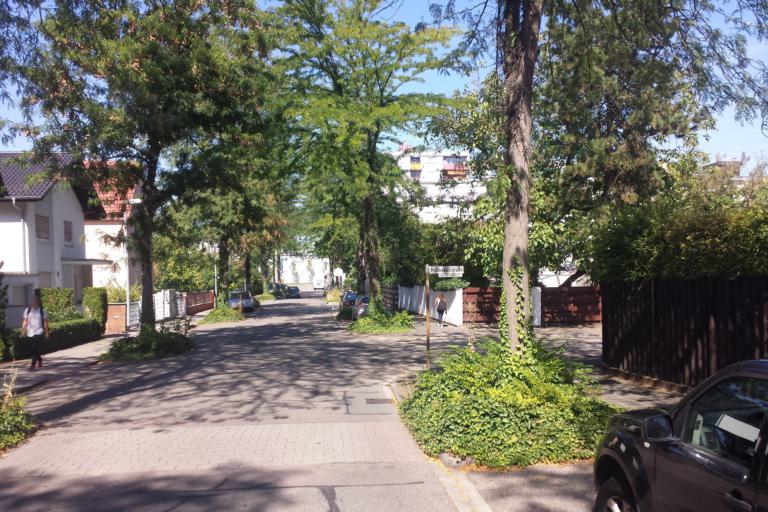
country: DE
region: Hesse
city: Viernheim
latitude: 49.5421
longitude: 8.5881
